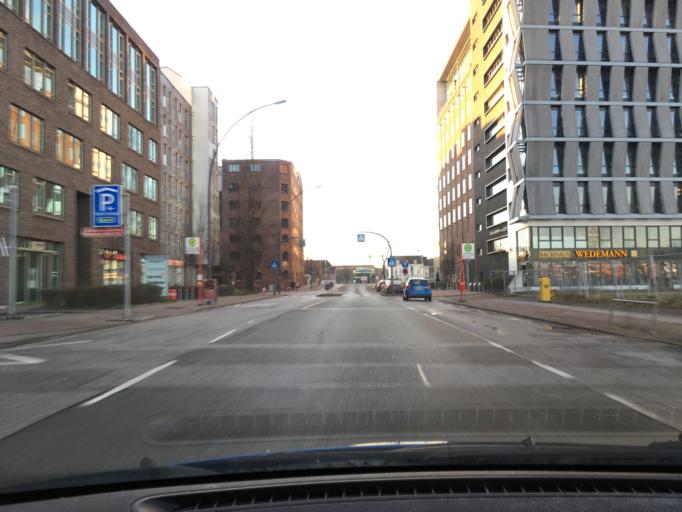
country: DE
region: Hamburg
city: Harburg
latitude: 53.4660
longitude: 9.9882
